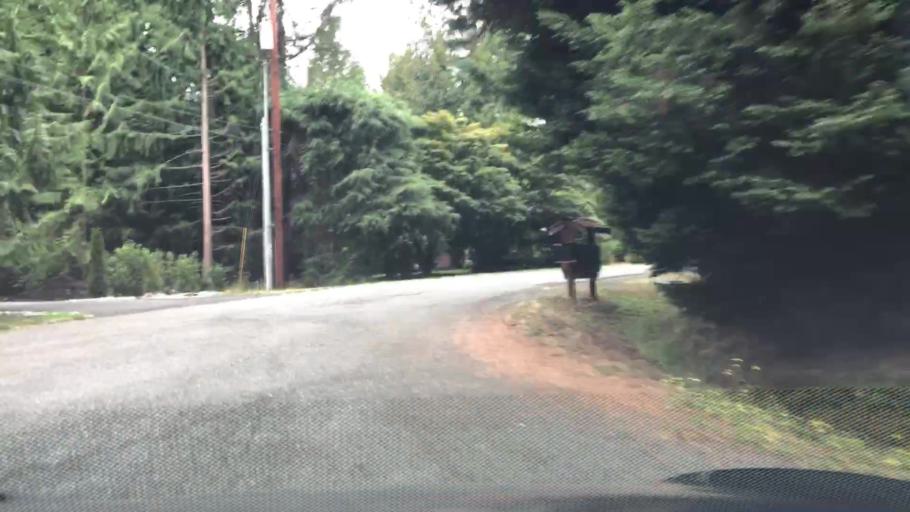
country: US
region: Washington
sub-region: King County
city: Cottage Lake
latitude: 47.7694
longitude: -122.0943
